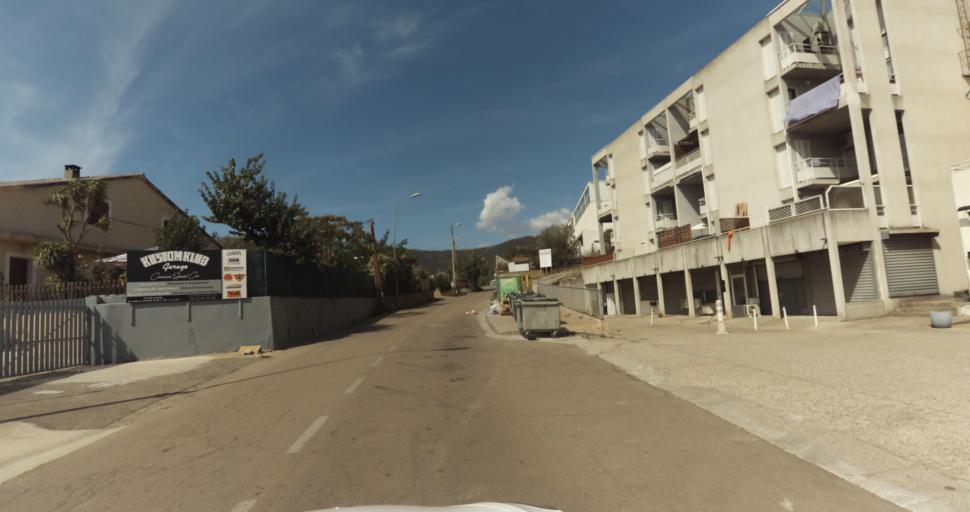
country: FR
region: Corsica
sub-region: Departement de la Corse-du-Sud
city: Afa
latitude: 41.9528
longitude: 8.7739
